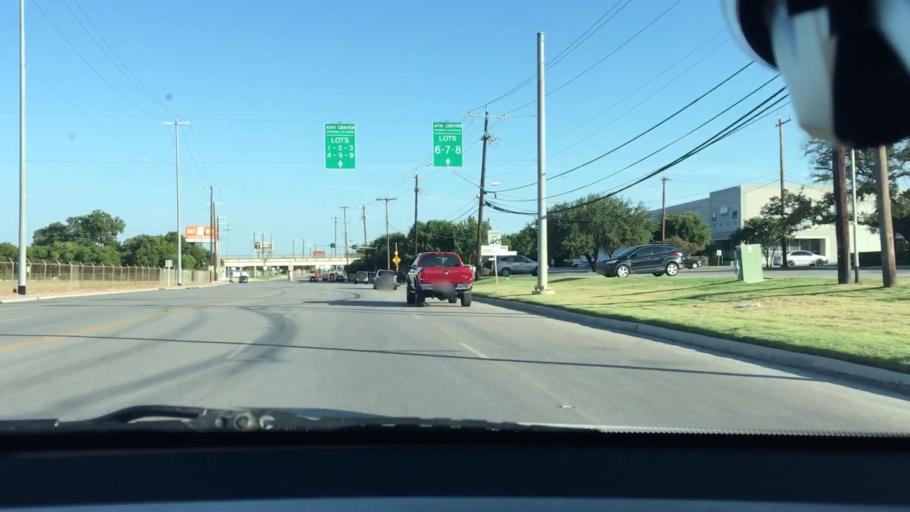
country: US
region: Texas
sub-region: Bexar County
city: Terrell Hills
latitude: 29.4405
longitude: -98.4371
